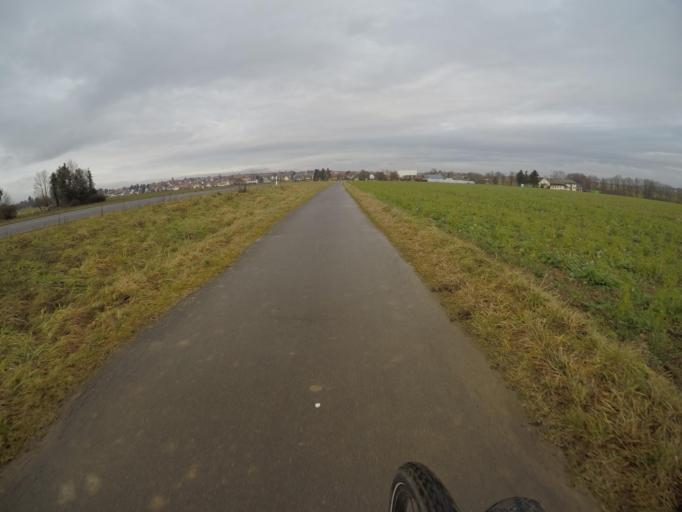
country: DE
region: Baden-Wuerttemberg
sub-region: Regierungsbezirk Stuttgart
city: Neckartailfingen
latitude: 48.6411
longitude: 9.2498
